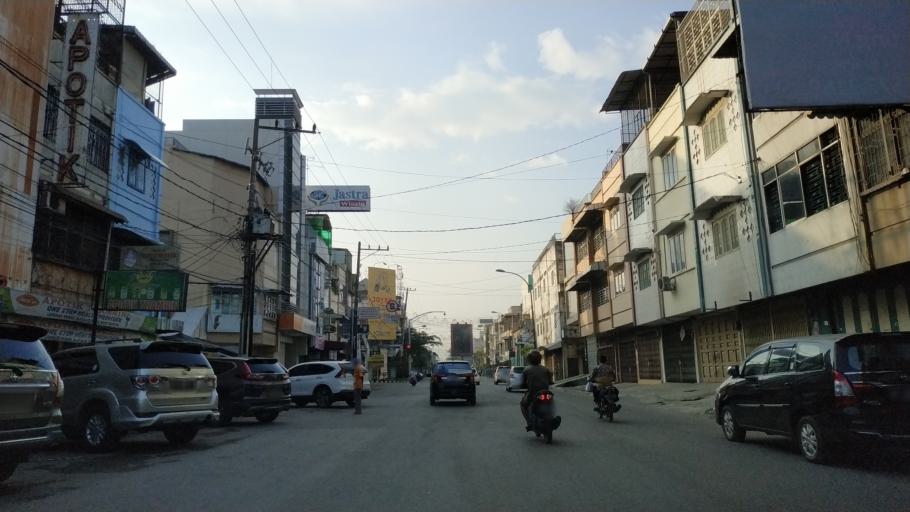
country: ID
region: North Sumatra
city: Medan
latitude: 3.5856
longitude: 98.6917
